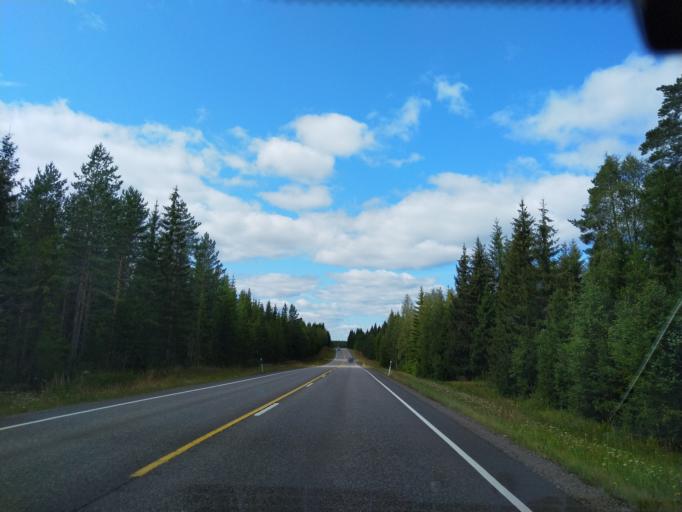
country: FI
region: Haeme
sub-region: Haemeenlinna
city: Renko
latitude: 60.7650
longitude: 24.2603
